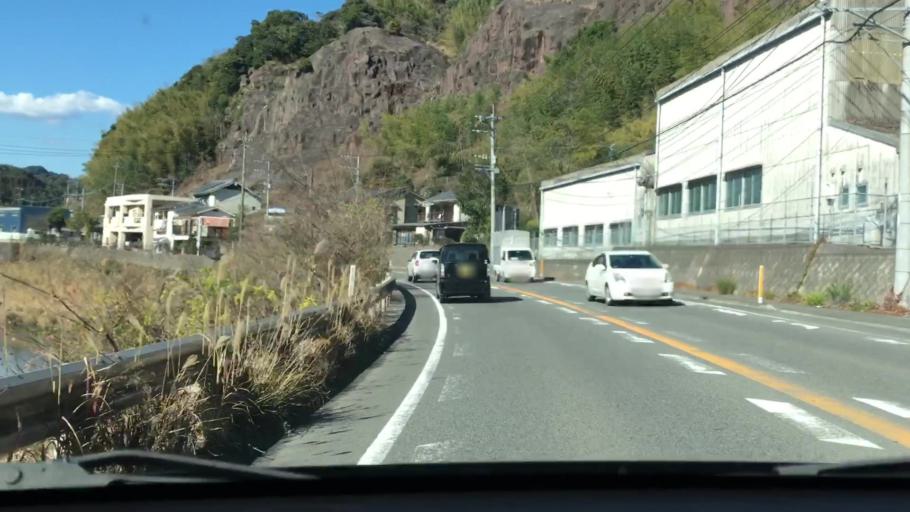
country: JP
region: Kagoshima
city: Kagoshima-shi
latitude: 31.6337
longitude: 130.5236
